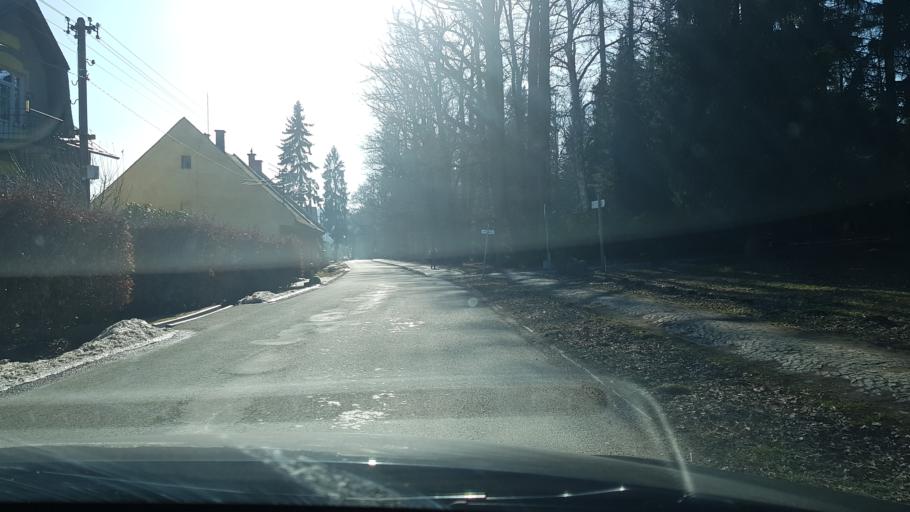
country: CZ
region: Olomoucky
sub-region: Okres Sumperk
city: Velke Losiny
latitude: 50.0345
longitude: 17.0399
